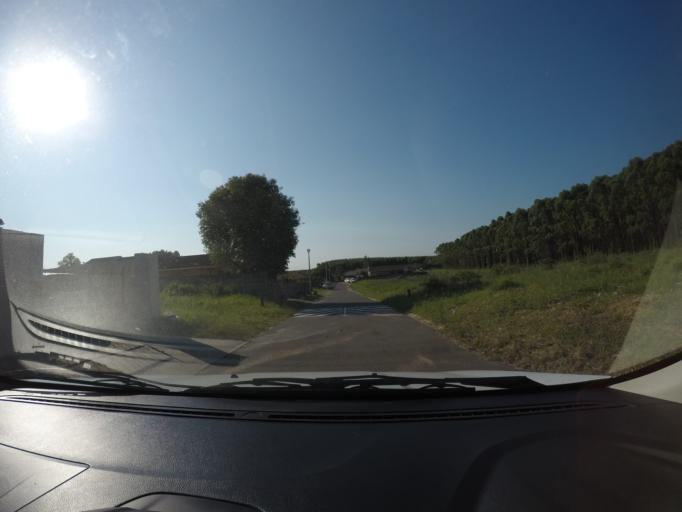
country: ZA
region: KwaZulu-Natal
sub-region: uThungulu District Municipality
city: Richards Bay
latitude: -28.7122
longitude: 32.0411
